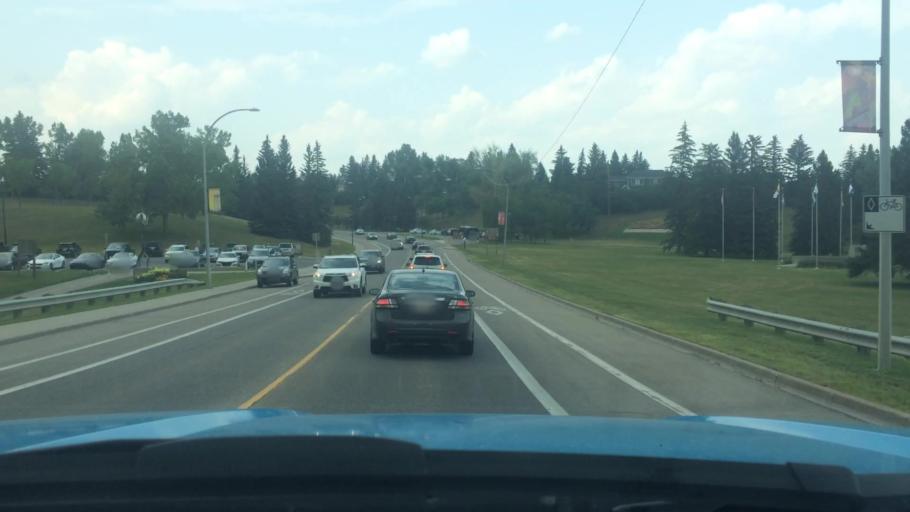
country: CA
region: Alberta
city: Calgary
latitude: 51.0758
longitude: -114.0846
